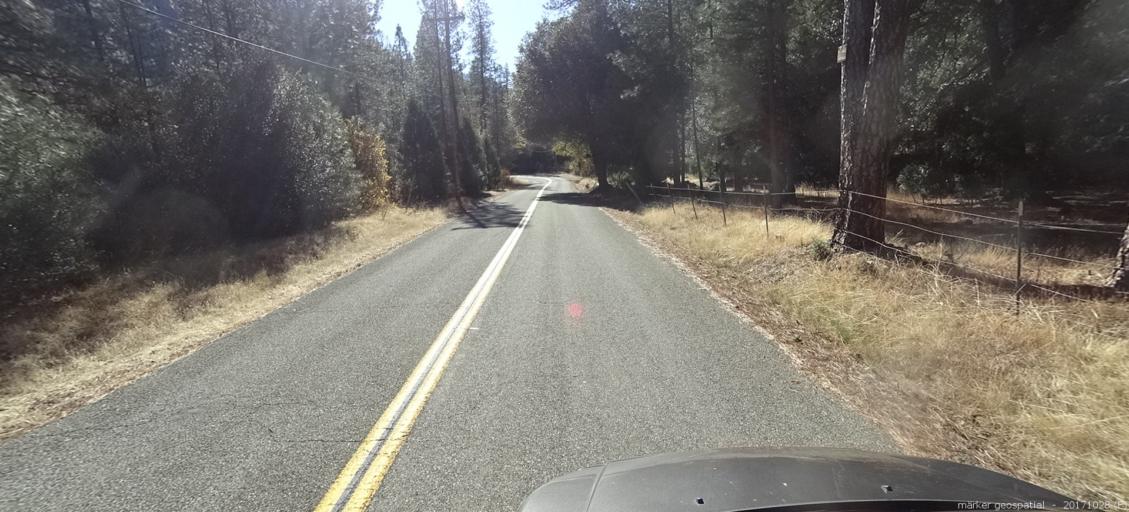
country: US
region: California
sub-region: Trinity County
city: Lewiston
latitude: 40.7792
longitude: -122.6122
